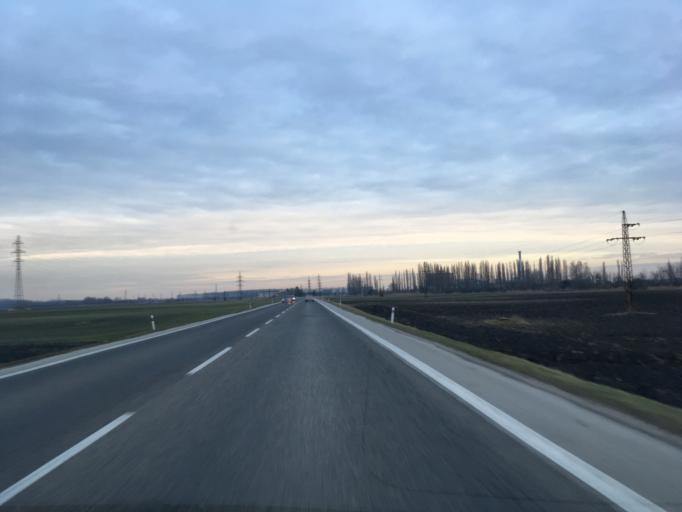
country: SK
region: Trnavsky
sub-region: Okres Dunajska Streda
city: Velky Meder
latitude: 47.8835
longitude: 17.7488
